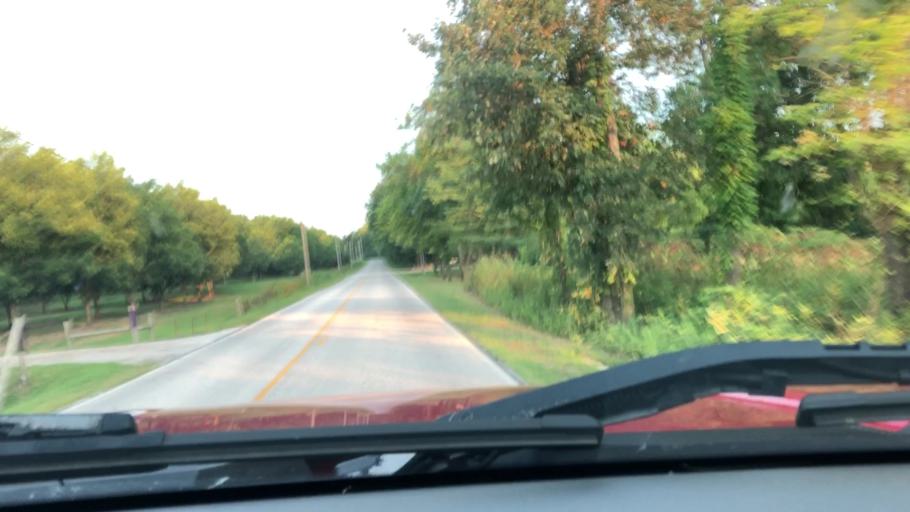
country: US
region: Missouri
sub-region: Jasper County
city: Joplin
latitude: 37.0201
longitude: -94.5098
